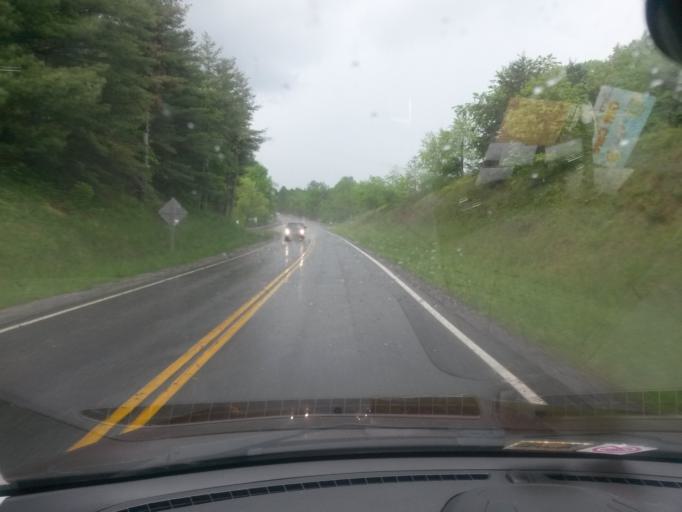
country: US
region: Virginia
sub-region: Floyd County
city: Floyd
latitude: 36.9655
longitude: -80.3746
